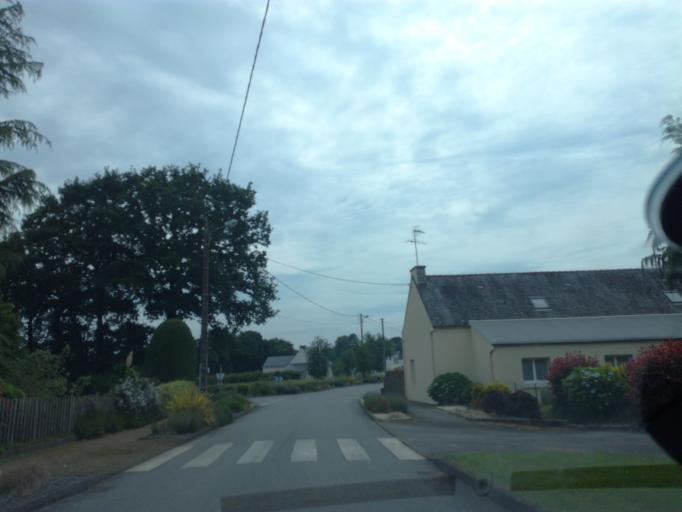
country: FR
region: Brittany
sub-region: Departement du Morbihan
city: Saint-Thuriau
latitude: 48.0211
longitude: -2.9542
